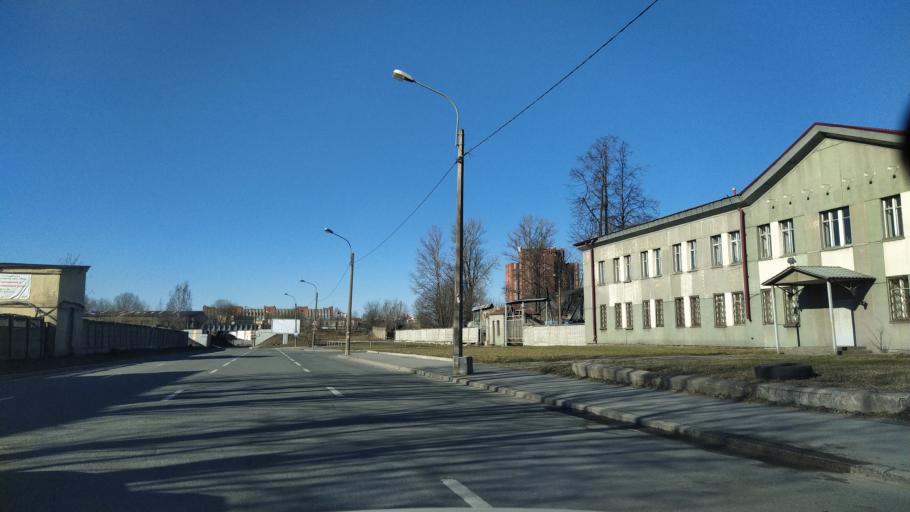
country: RU
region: St.-Petersburg
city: Centralniy
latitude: 59.9103
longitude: 30.3756
